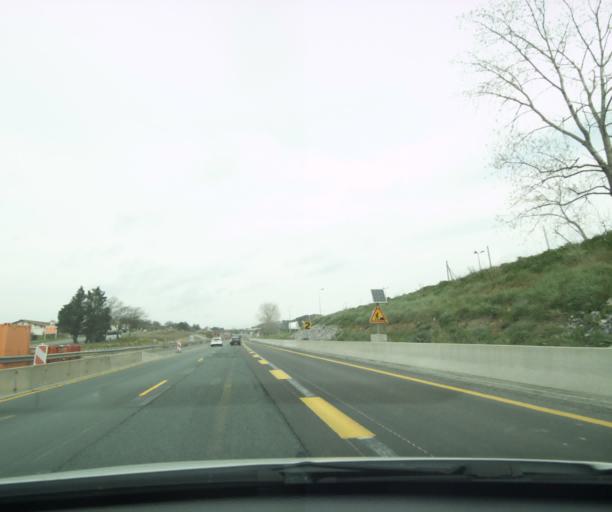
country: FR
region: Aquitaine
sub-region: Departement des Pyrenees-Atlantiques
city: Guethary
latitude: 43.4053
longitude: -1.6293
